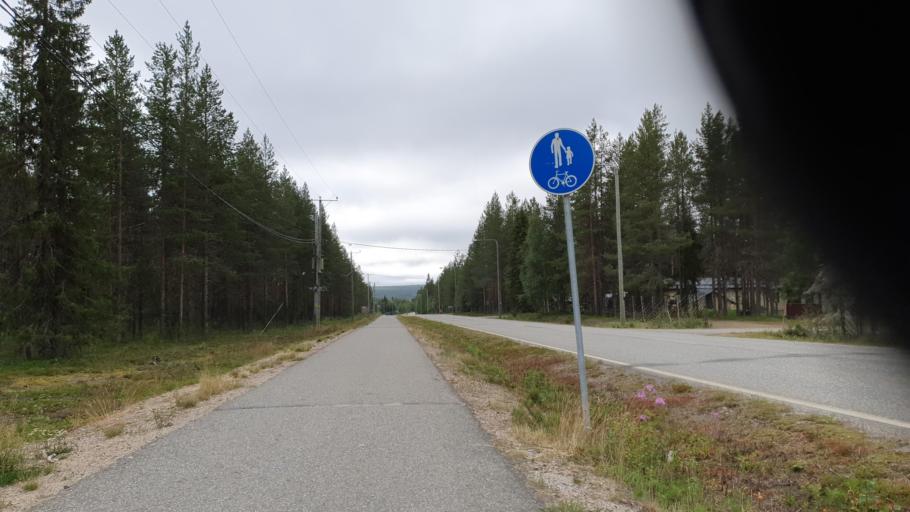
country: FI
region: Lapland
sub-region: Tunturi-Lappi
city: Kolari
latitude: 67.6225
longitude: 24.1546
